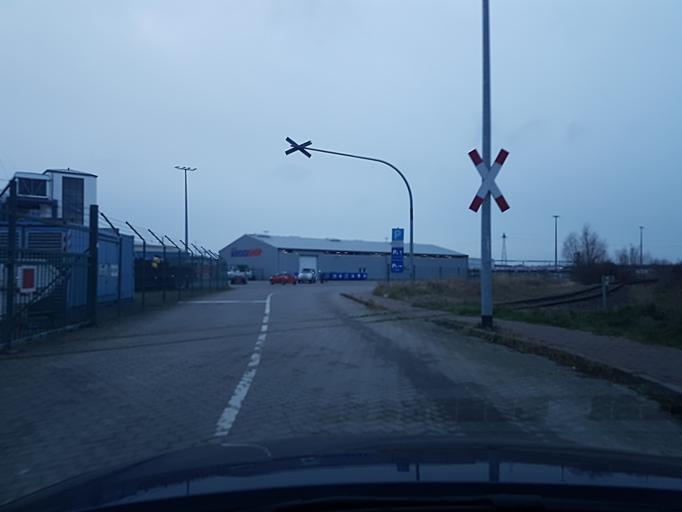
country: DE
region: Mecklenburg-Vorpommern
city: Sagard
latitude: 54.4862
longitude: 13.5889
